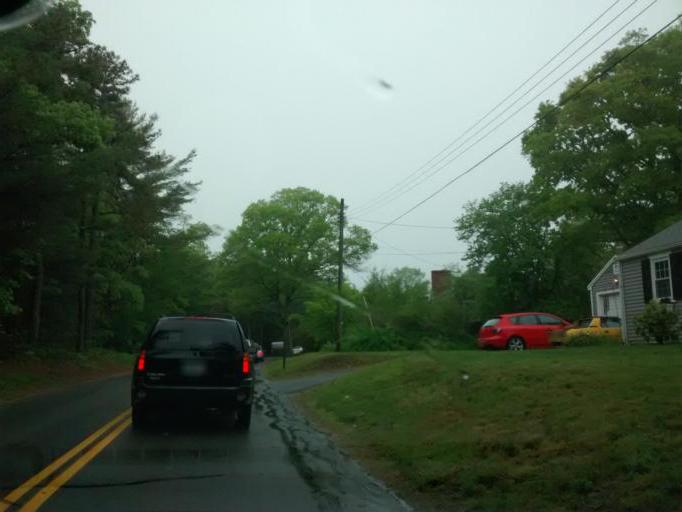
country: US
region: Massachusetts
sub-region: Barnstable County
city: Pocasset
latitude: 41.6887
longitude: -70.5994
